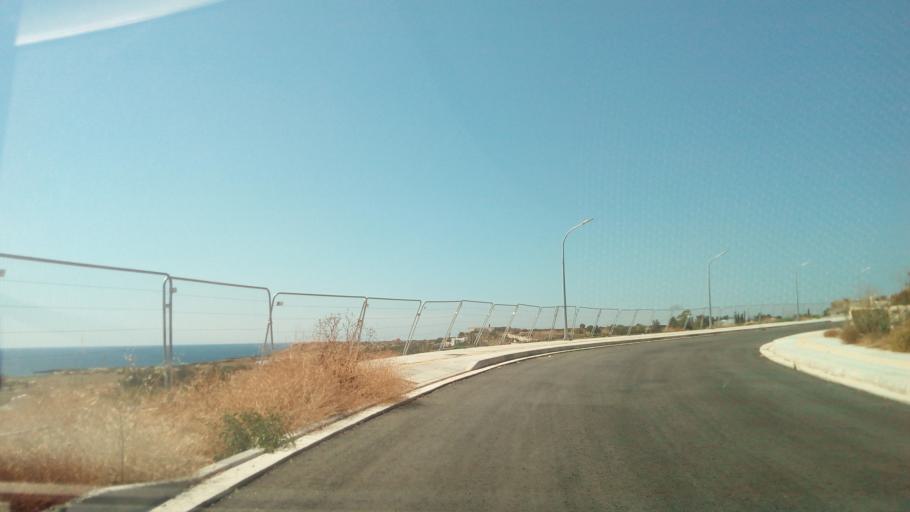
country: CY
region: Pafos
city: Pegeia
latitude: 34.8947
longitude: 32.3263
